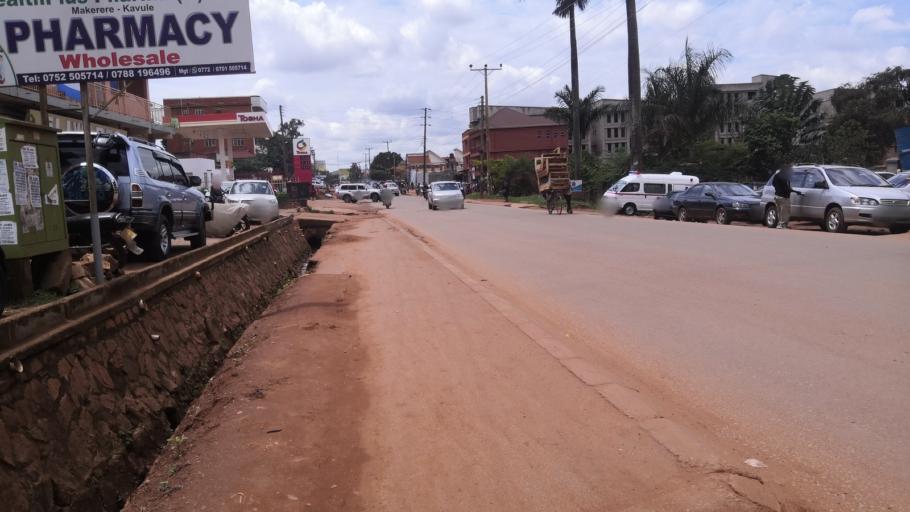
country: UG
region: Central Region
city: Kampala Central Division
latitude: 0.3441
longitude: 32.5695
